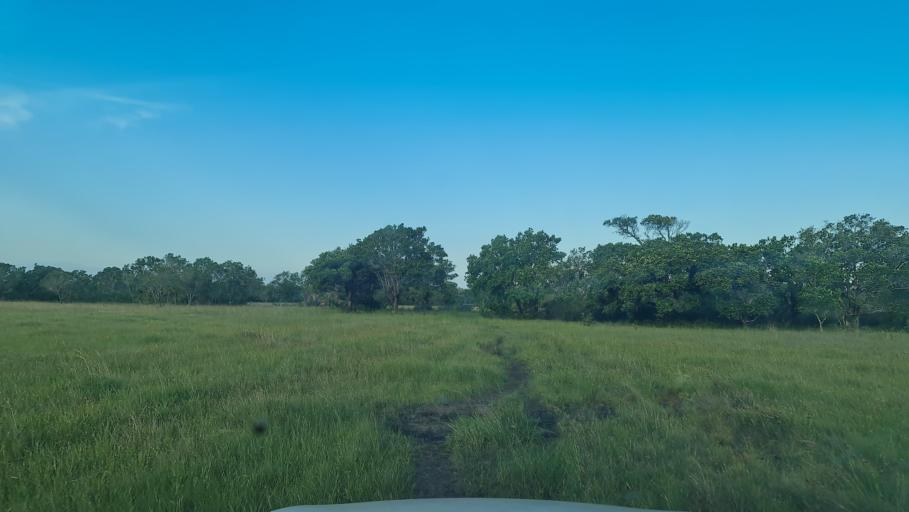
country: MZ
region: Gaza
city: Macia
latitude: -25.2220
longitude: 33.0302
